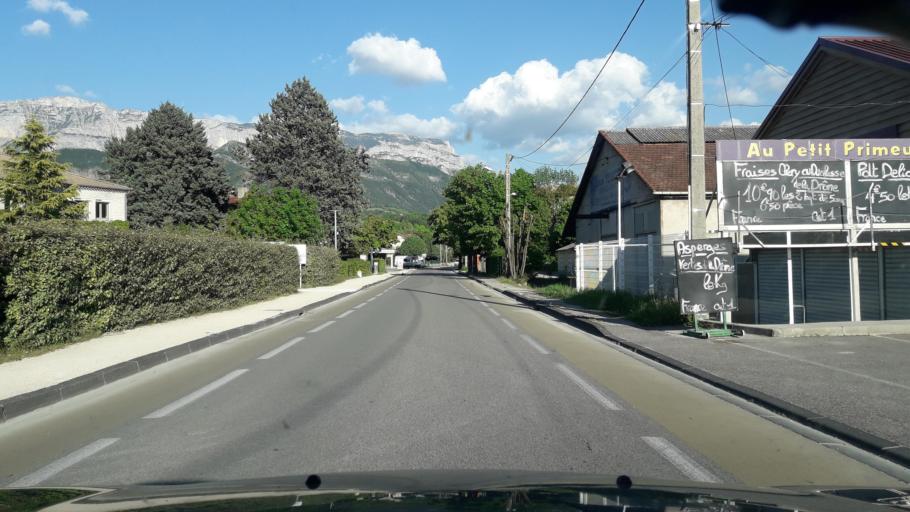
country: FR
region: Rhone-Alpes
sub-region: Departement de la Drome
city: Die
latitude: 44.7602
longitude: 5.3591
